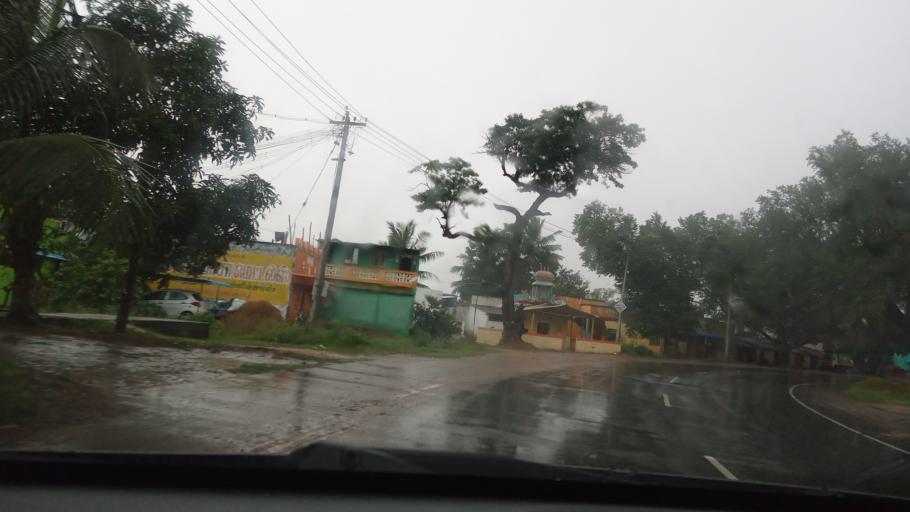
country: IN
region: Tamil Nadu
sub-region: Vellore
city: Kalavai
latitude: 12.8049
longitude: 79.4150
